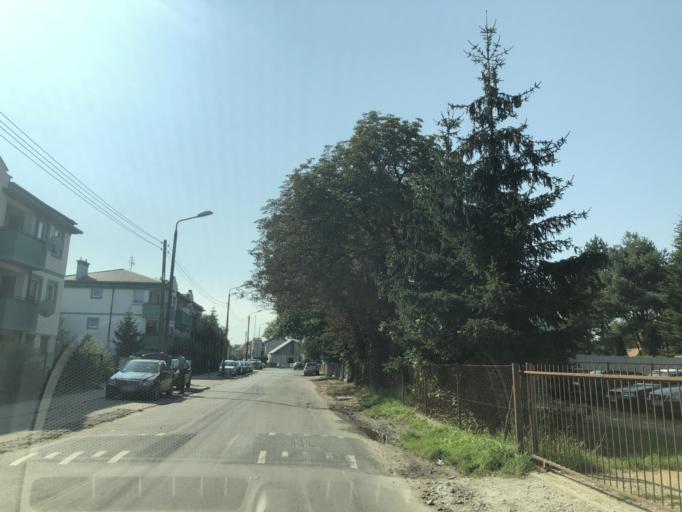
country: PL
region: Lower Silesian Voivodeship
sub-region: Powiat wroclawski
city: Smolec
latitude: 51.1588
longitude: 16.9275
